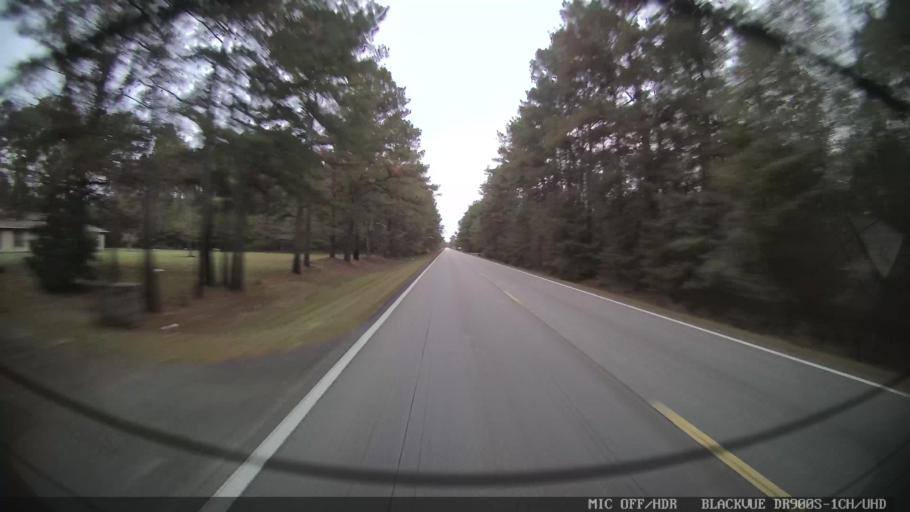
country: US
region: Mississippi
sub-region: Clarke County
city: Stonewall
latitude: 32.0307
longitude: -88.8669
